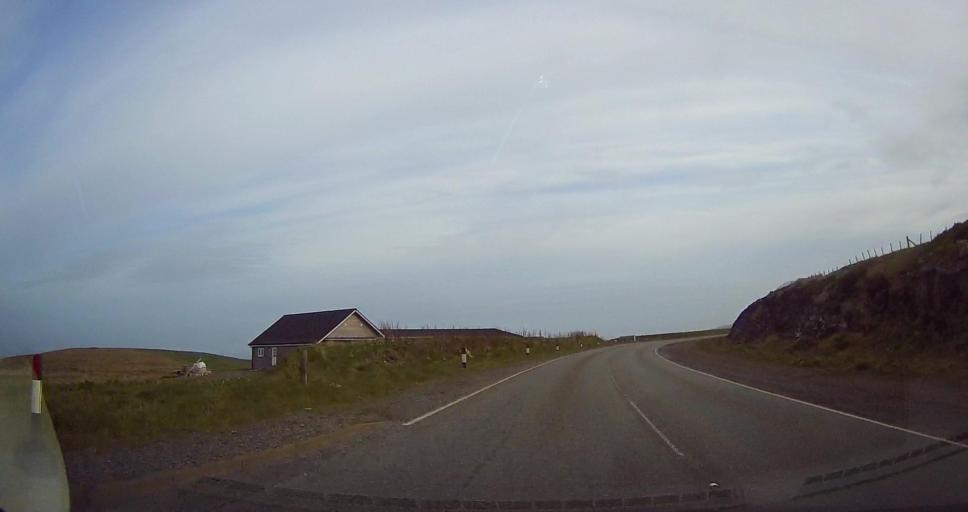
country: GB
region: Scotland
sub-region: Shetland Islands
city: Lerwick
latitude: 60.1215
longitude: -1.2153
